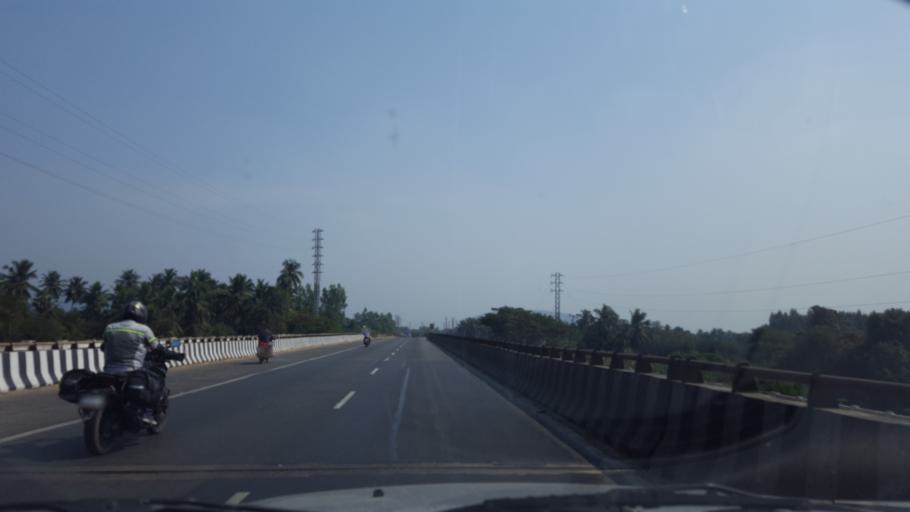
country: IN
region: Andhra Pradesh
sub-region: Vishakhapatnam
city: Anakapalle
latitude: 17.6799
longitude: 82.9917
